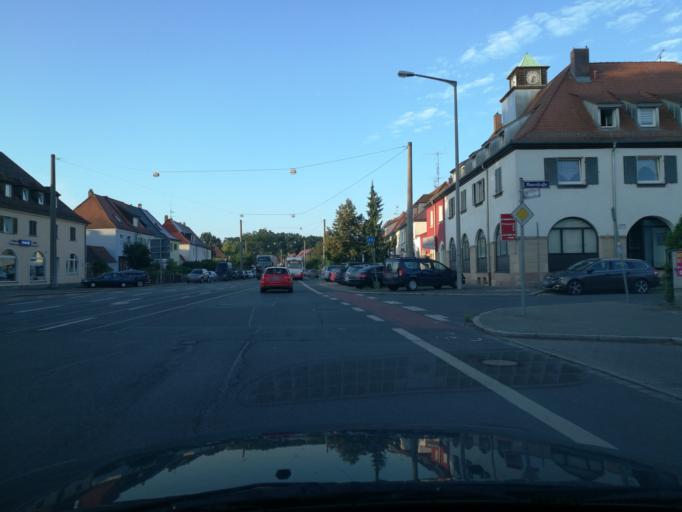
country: DE
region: Bavaria
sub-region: Regierungsbezirk Mittelfranken
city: Nuernberg
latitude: 49.4838
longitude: 11.1050
